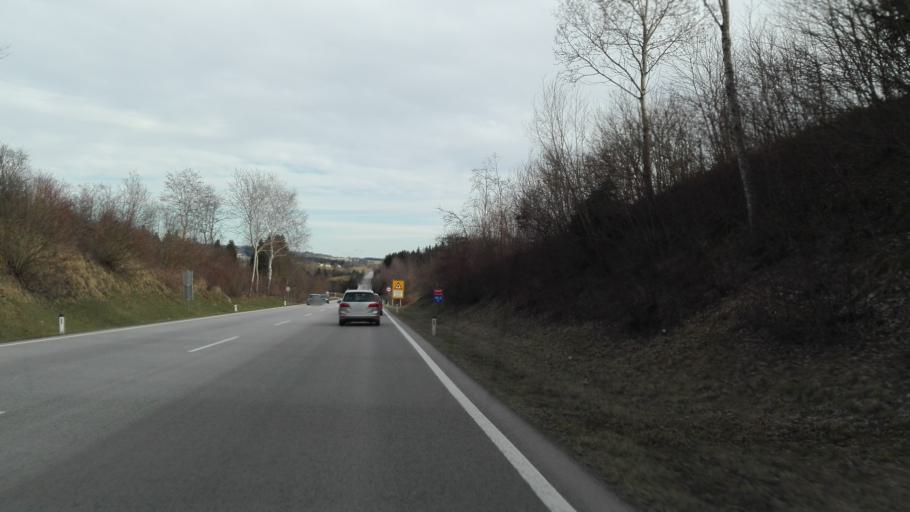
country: AT
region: Upper Austria
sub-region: Politischer Bezirk Rohrbach
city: Kleinzell im Muehlkreis
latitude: 48.4814
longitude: 13.9865
